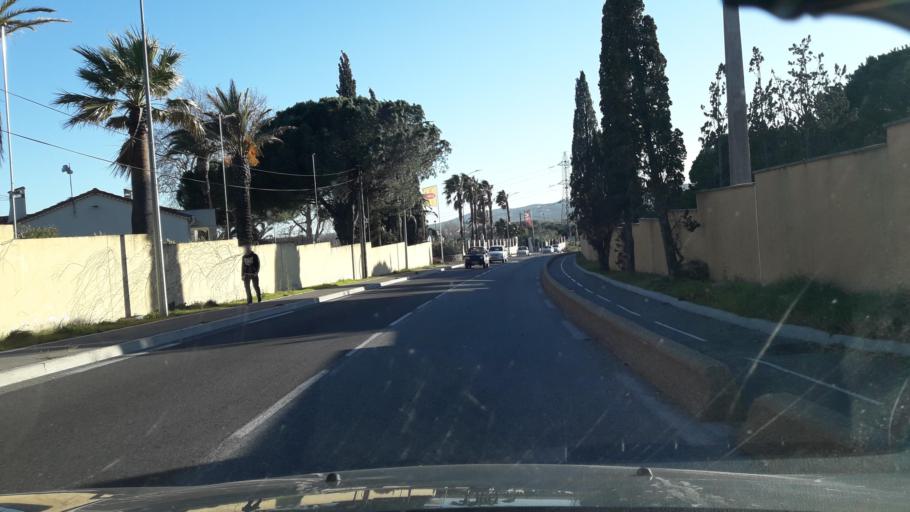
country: FR
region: Provence-Alpes-Cote d'Azur
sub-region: Departement du Var
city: Frejus
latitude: 43.4468
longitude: 6.7270
